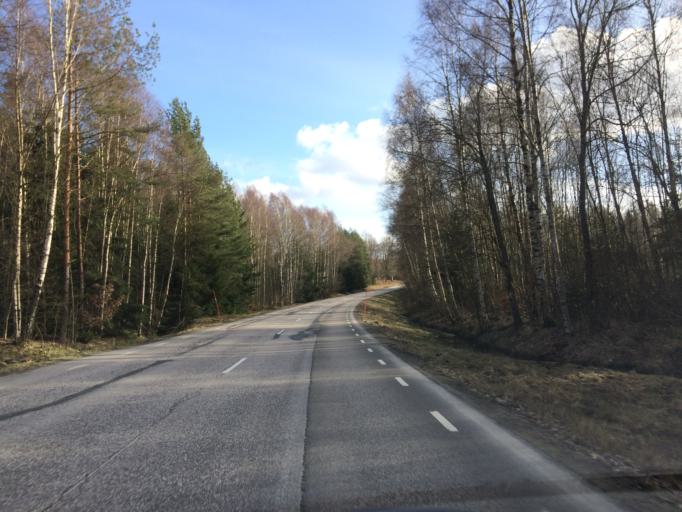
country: SE
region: Kronoberg
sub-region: Almhults Kommun
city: AElmhult
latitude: 56.6145
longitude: 14.0637
